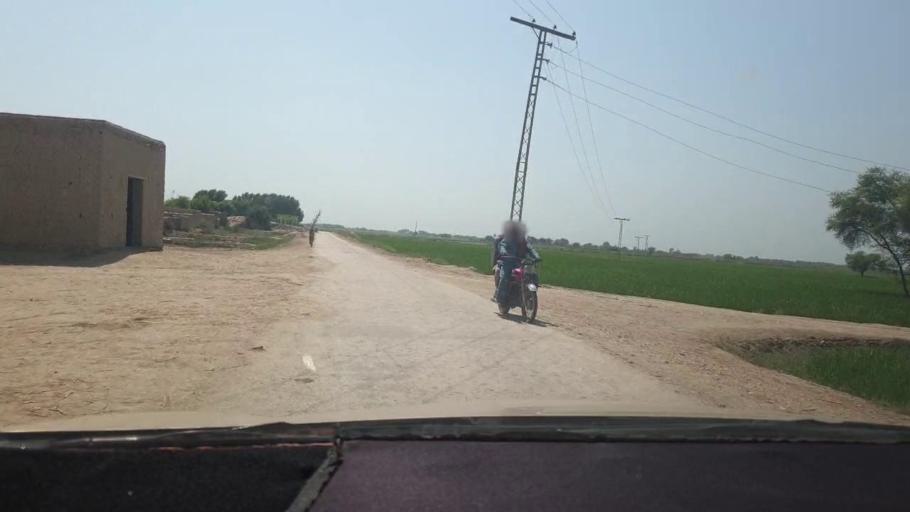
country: PK
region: Sindh
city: Miro Khan
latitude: 27.6619
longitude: 68.0788
